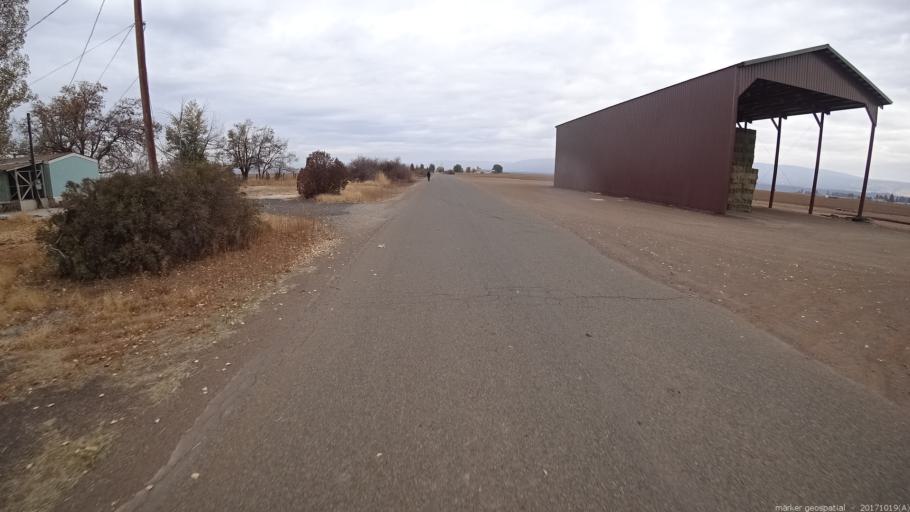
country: US
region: California
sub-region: Shasta County
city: Burney
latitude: 41.0595
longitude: -121.3891
